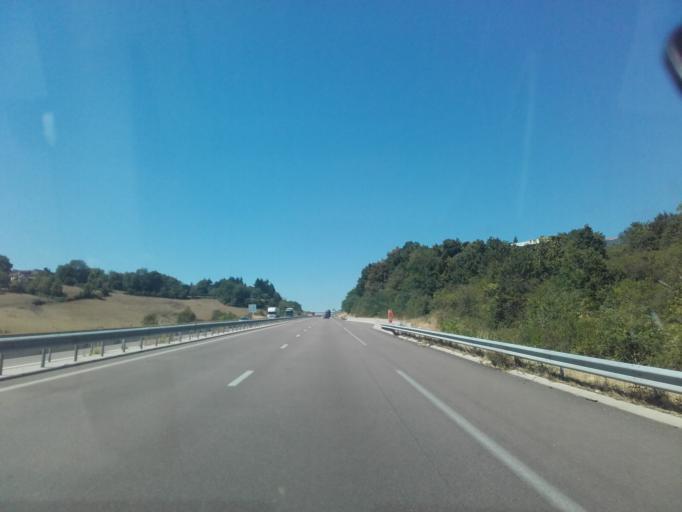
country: FR
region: Bourgogne
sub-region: Departement de Saone-et-Loire
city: Buxy
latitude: 46.7547
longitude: 4.6855
